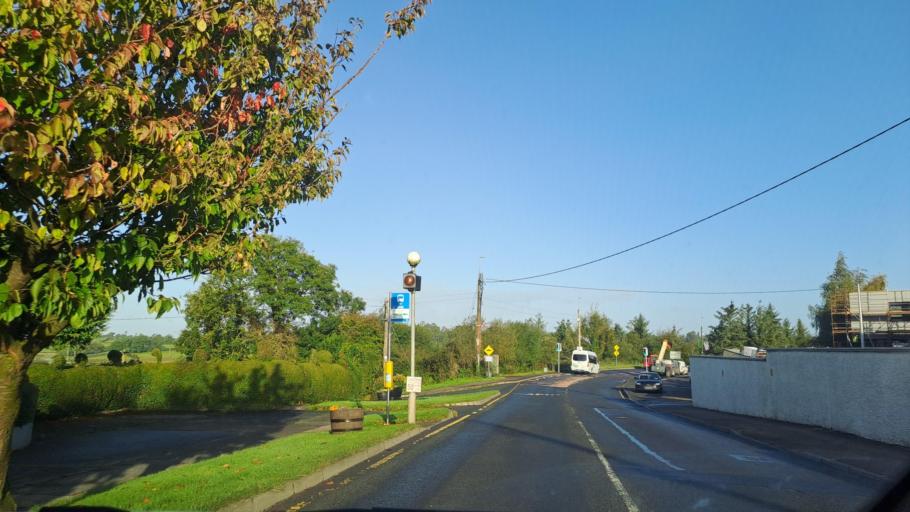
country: IE
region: Ulster
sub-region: County Monaghan
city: Monaghan
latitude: 54.1229
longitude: -6.9015
